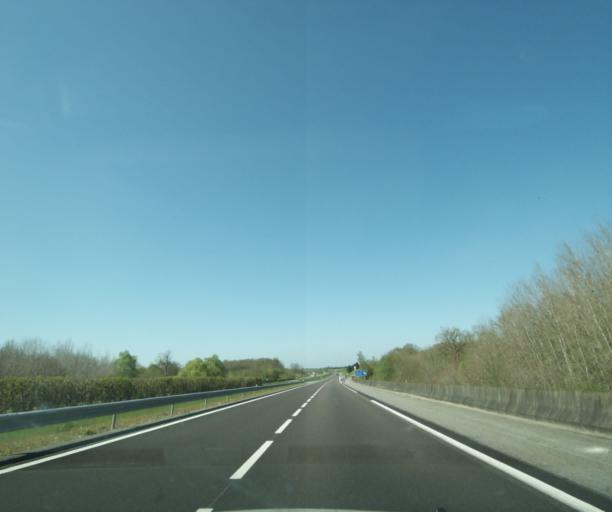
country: FR
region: Bourgogne
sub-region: Departement de la Nievre
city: Neuvy-sur-Loire
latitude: 47.5060
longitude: 2.9219
